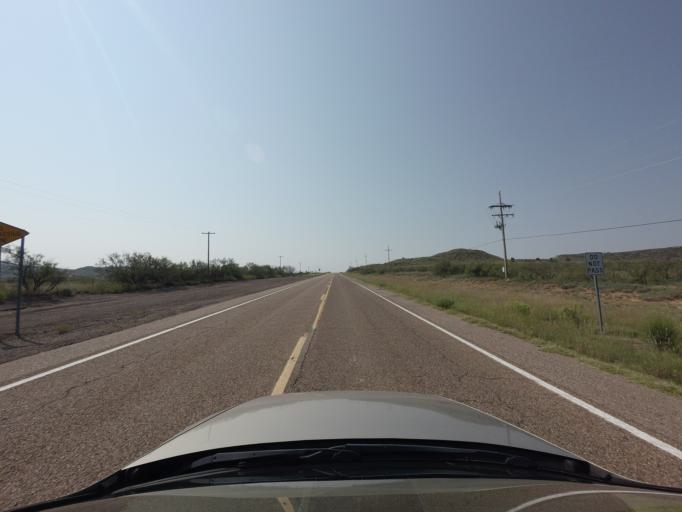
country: US
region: New Mexico
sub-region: Quay County
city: Tucumcari
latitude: 35.1419
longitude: -103.7250
